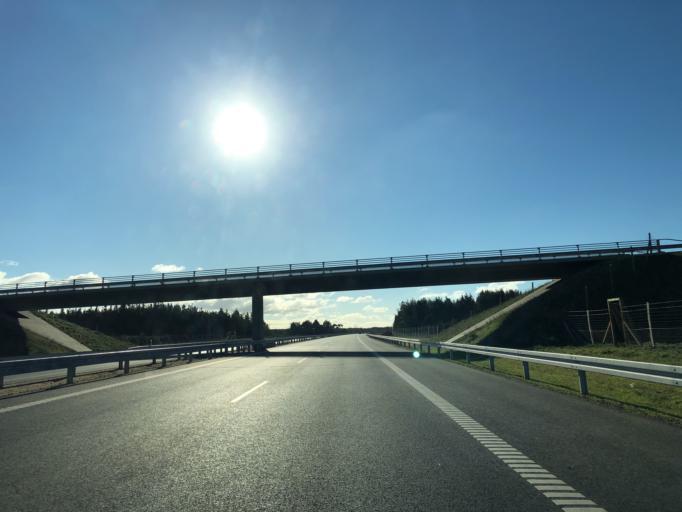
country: DK
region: Central Jutland
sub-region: Herning Kommune
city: Avlum
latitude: 56.3383
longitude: 8.7378
